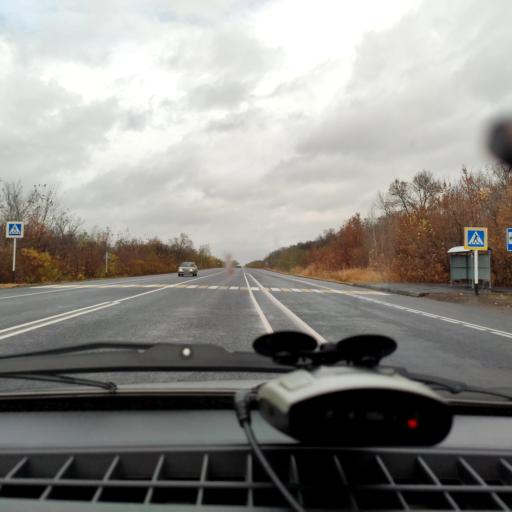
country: RU
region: Voronezj
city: Uryv-Pokrovka
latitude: 51.2318
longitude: 39.0594
